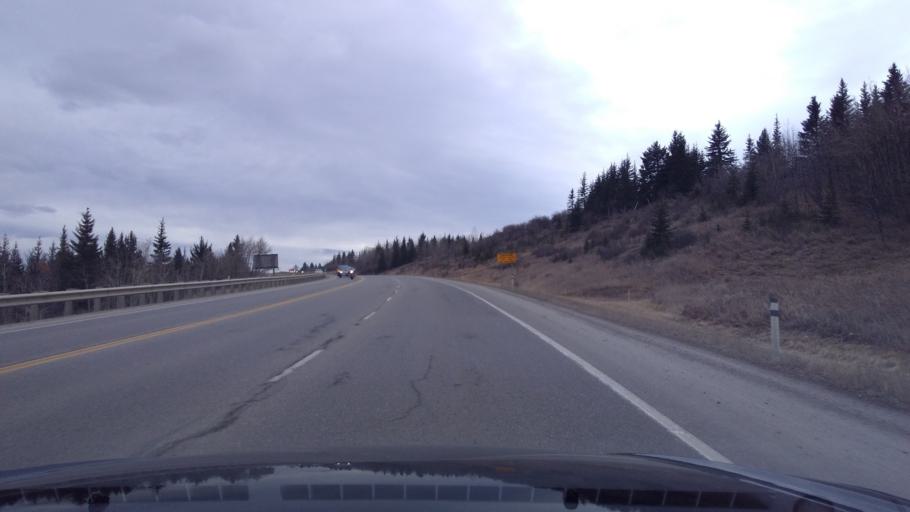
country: CA
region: Alberta
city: Cochrane
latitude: 51.1780
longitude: -114.4872
